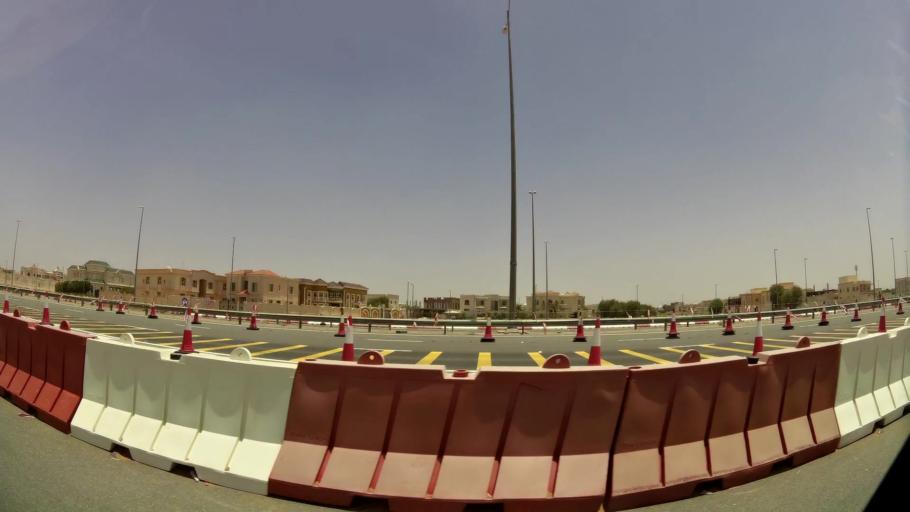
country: OM
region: Al Buraimi
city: Al Buraymi
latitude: 24.2734
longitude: 55.7124
